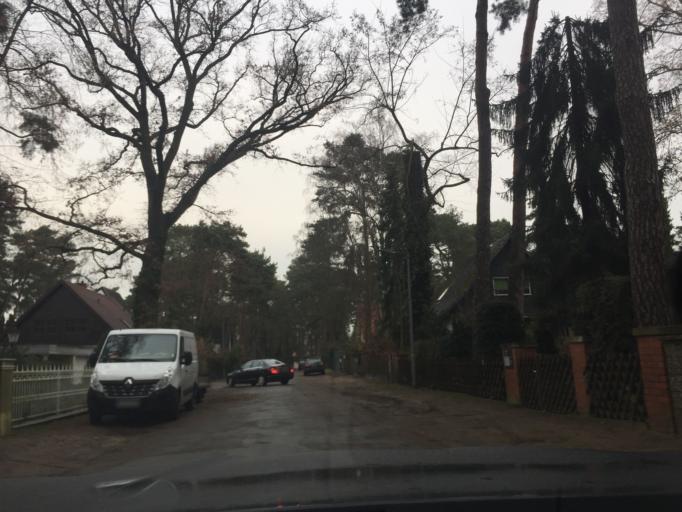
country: DE
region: Berlin
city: Kladow
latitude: 52.4684
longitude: 13.1191
